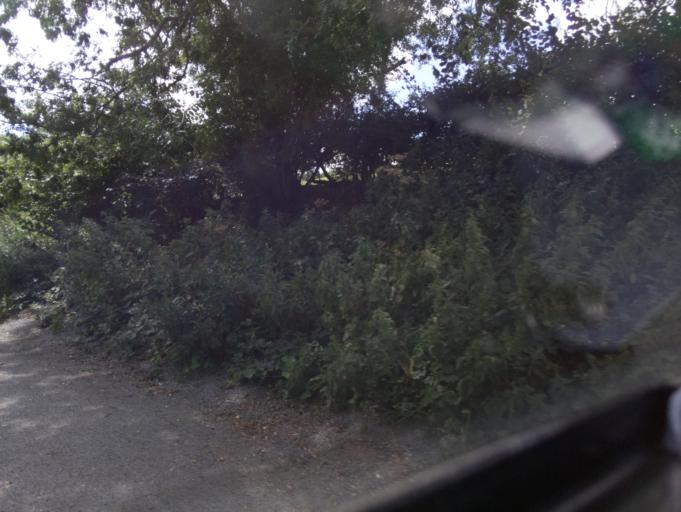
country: GB
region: England
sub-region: Nottinghamshire
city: Lowdham
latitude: 53.0001
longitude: -1.0162
